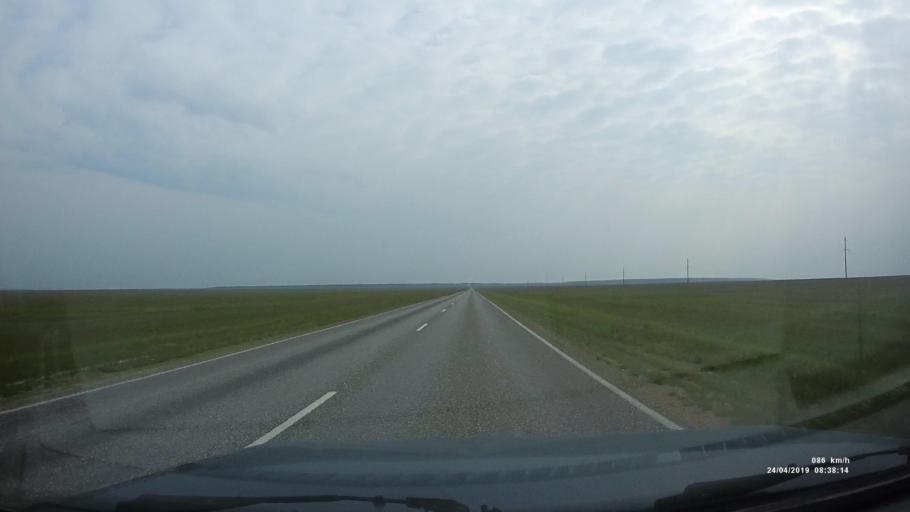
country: RU
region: Kalmykiya
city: Arshan'
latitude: 46.2143
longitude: 43.9639
